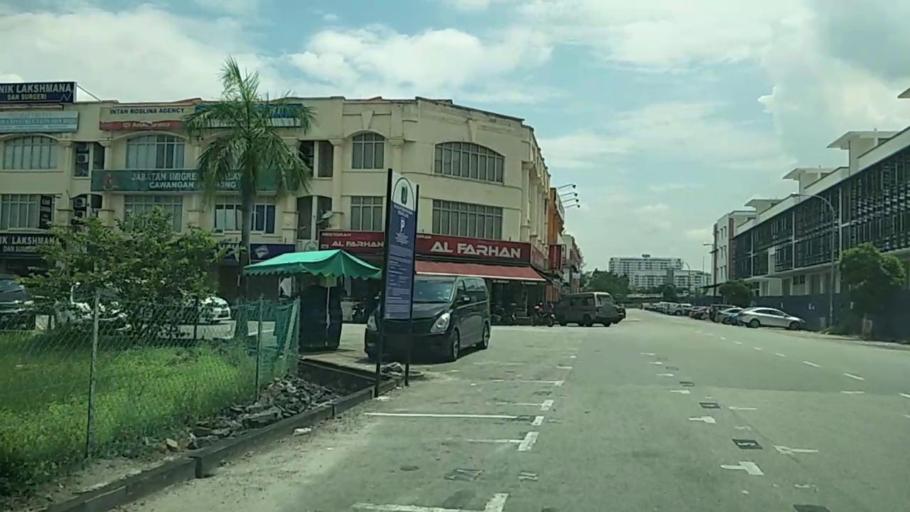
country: MY
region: Selangor
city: Subang Jaya
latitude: 2.9908
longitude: 101.6168
